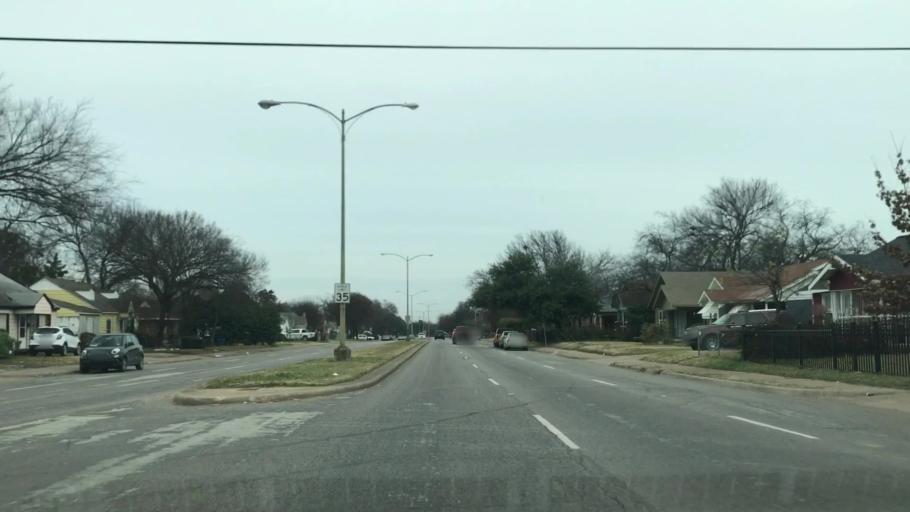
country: US
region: Texas
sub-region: Dallas County
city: Dallas
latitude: 32.7277
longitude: -96.8144
